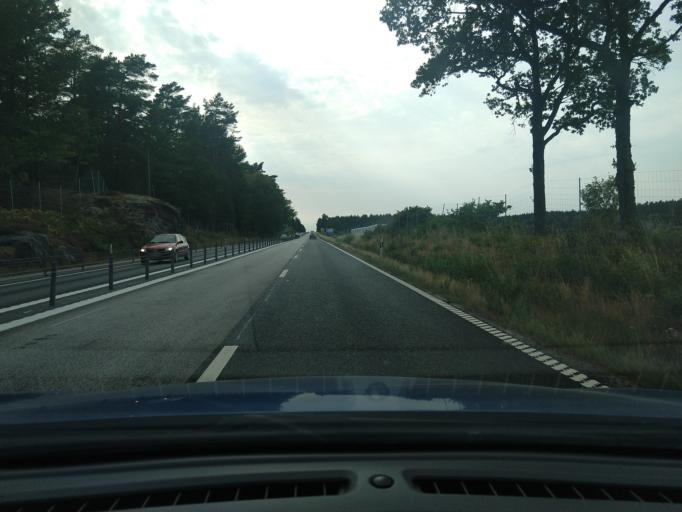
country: SE
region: Blekinge
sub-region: Karlskrona Kommun
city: Nattraby
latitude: 56.1984
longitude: 15.4237
